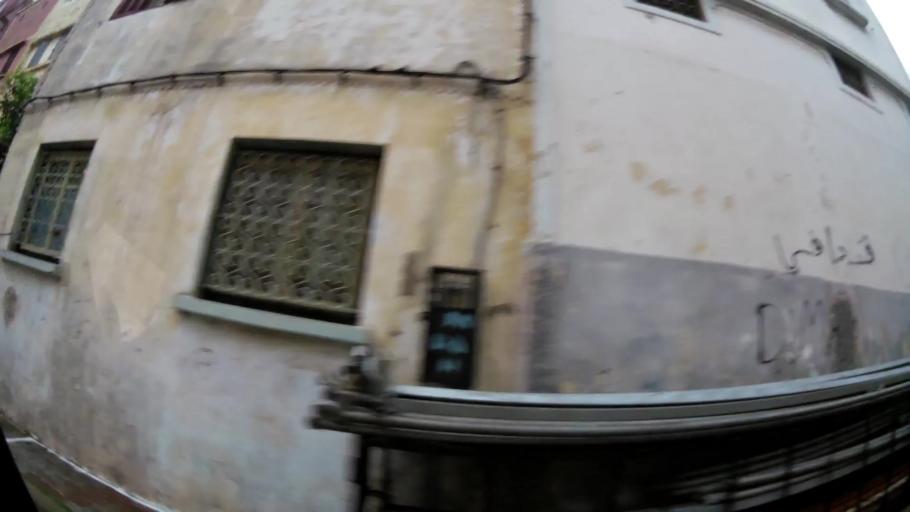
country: MA
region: Grand Casablanca
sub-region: Casablanca
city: Casablanca
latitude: 33.5539
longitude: -7.5849
